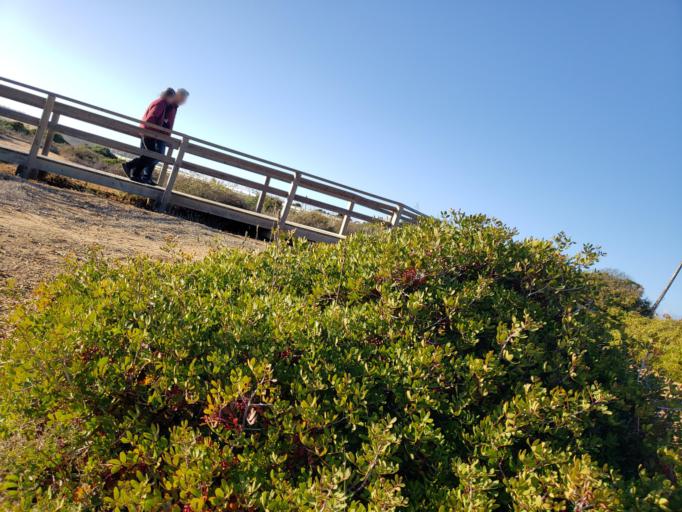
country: PT
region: Faro
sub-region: Lagos
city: Lagos
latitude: 37.0824
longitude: -8.6746
